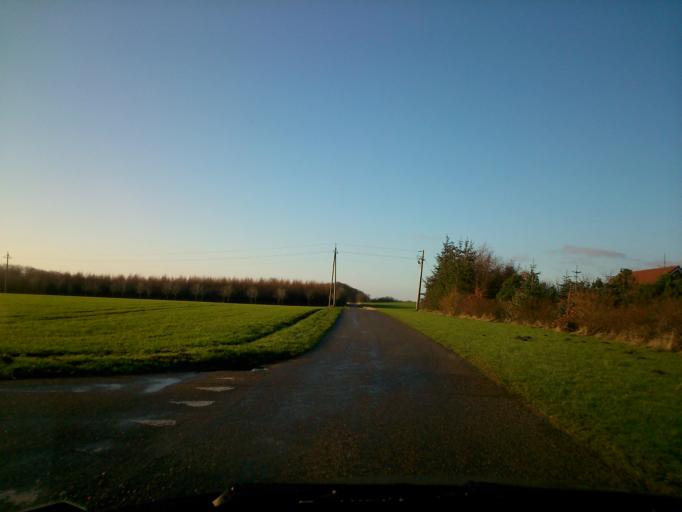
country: DK
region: Central Jutland
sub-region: Ringkobing-Skjern Kommune
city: Skjern
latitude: 55.9801
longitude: 8.5476
